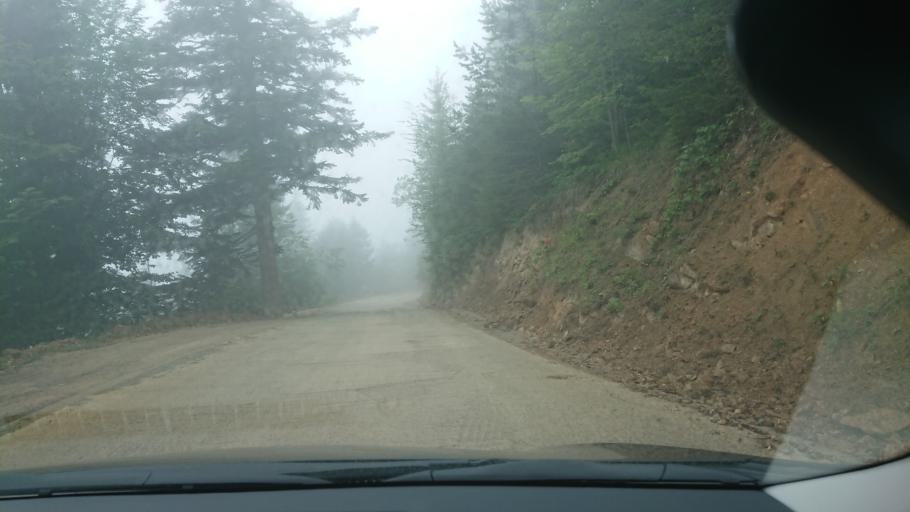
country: TR
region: Gumushane
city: Kurtun
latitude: 40.6619
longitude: 39.0194
